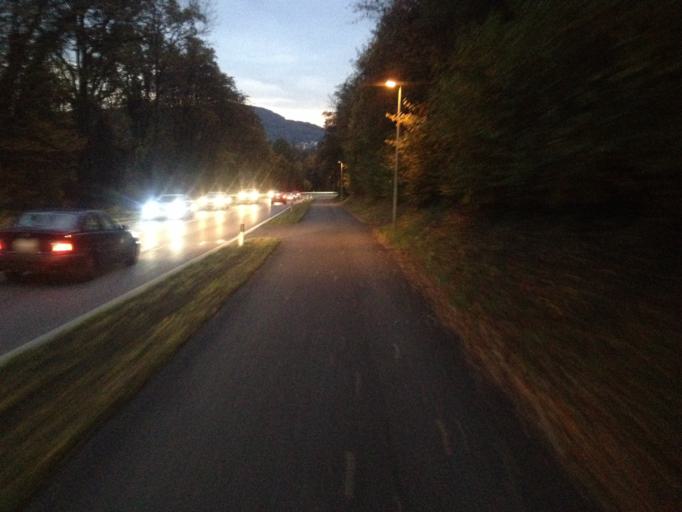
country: CH
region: Aargau
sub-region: Bezirk Brugg
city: Lauffohr (Brugg)
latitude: 47.5074
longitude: 8.2316
